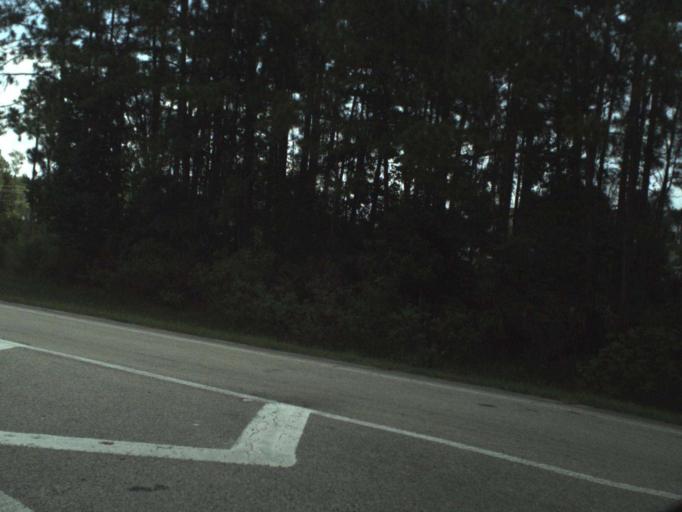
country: US
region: Florida
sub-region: Volusia County
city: South Daytona
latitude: 29.1563
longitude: -81.0734
